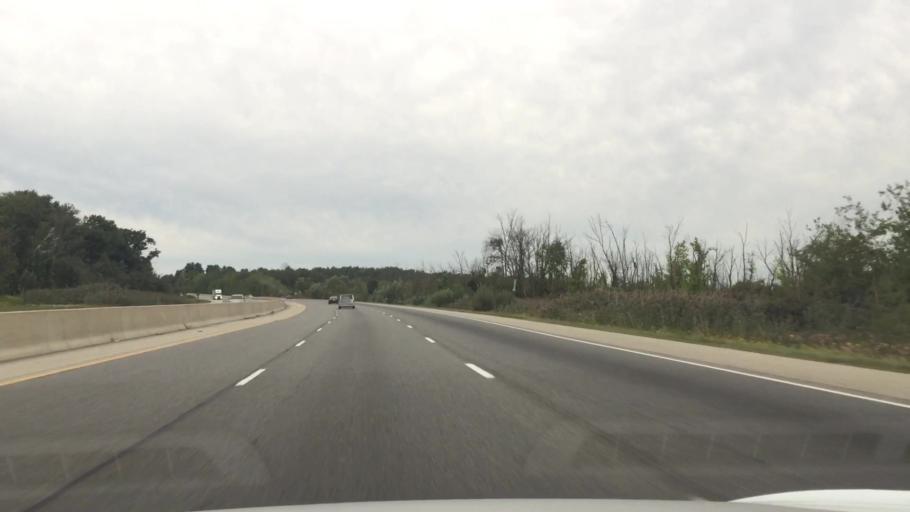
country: CA
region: Ontario
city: Kitchener
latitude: 43.2600
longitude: -80.5632
